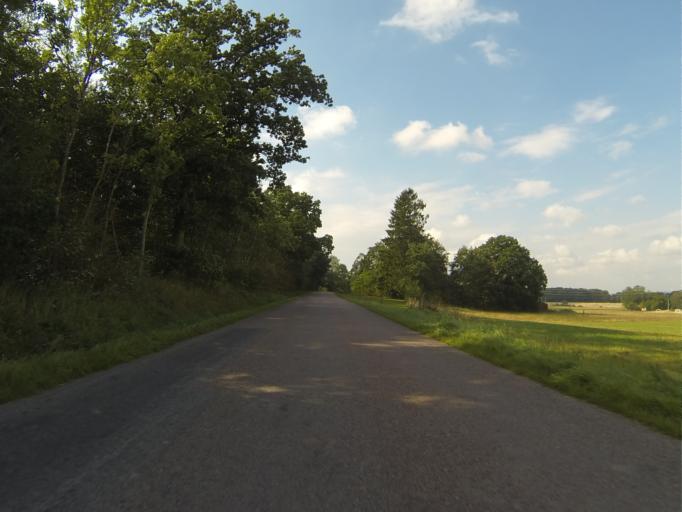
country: SE
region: Skane
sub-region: Eslovs Kommun
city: Eslov
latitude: 55.7248
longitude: 13.3139
